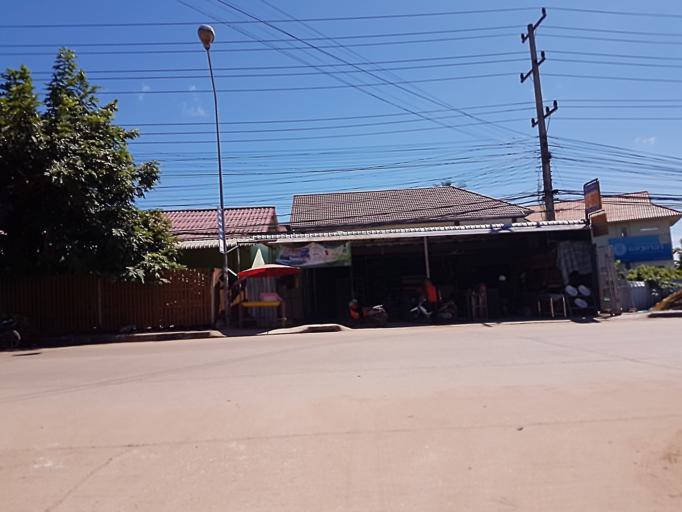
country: LA
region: Vientiane
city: Vientiane
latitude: 17.9430
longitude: 102.6298
